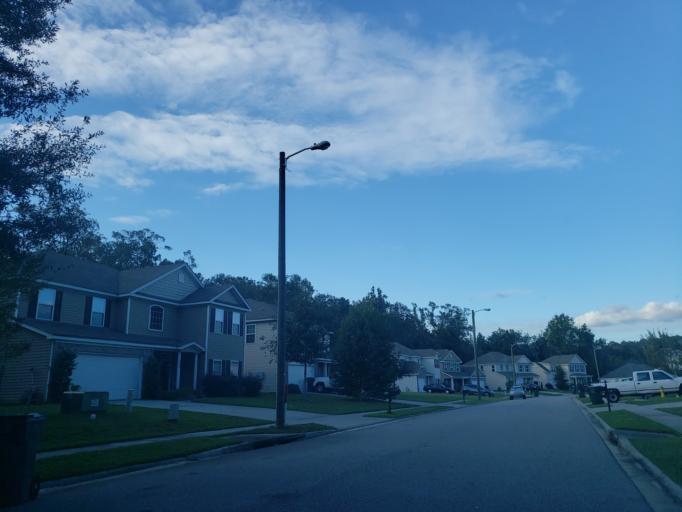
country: US
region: Georgia
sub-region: Chatham County
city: Georgetown
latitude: 31.9951
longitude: -81.2445
